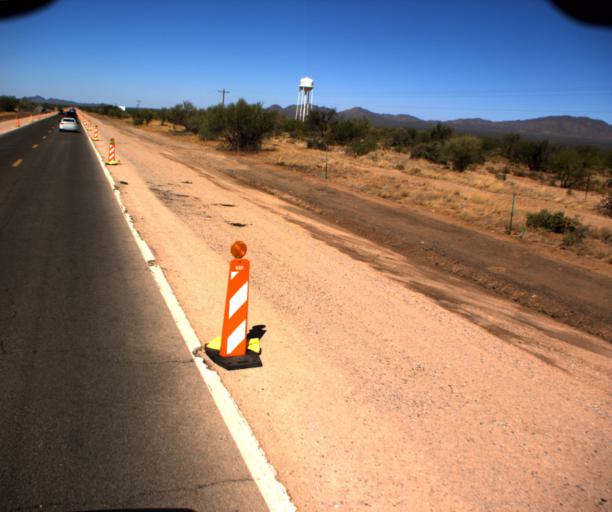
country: US
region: Arizona
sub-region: Pima County
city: Sells
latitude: 31.9920
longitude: -111.7075
